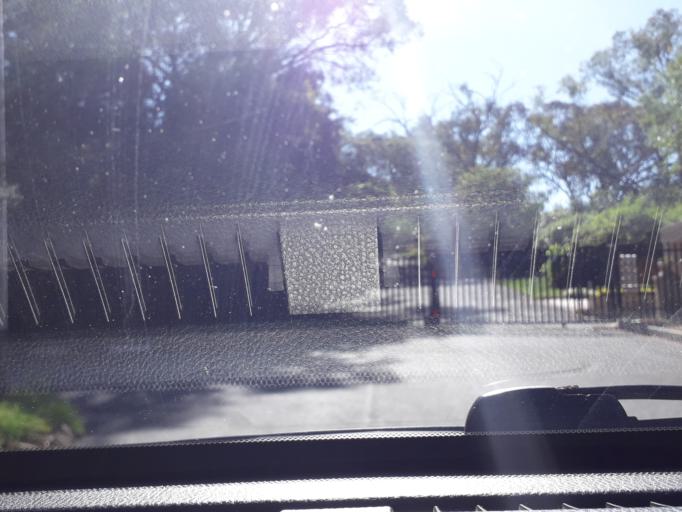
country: ZA
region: Gauteng
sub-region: City of Johannesburg Metropolitan Municipality
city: Johannesburg
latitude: -26.1278
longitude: 28.0293
